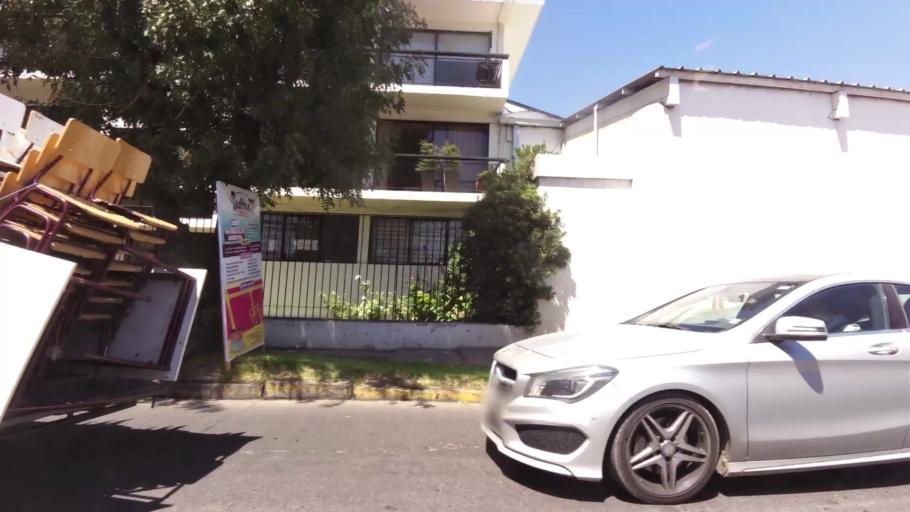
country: CL
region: Maule
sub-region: Provincia de Curico
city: Curico
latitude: -34.9836
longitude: -71.2182
